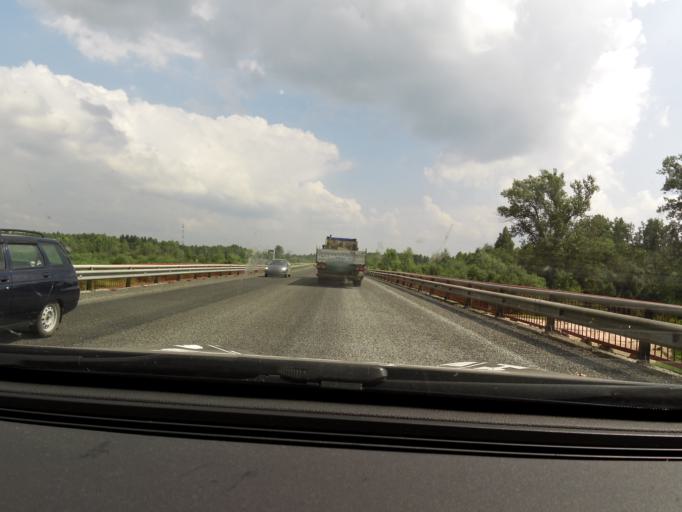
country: RU
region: Sverdlovsk
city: Ufimskiy
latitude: 56.7664
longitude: 58.1342
